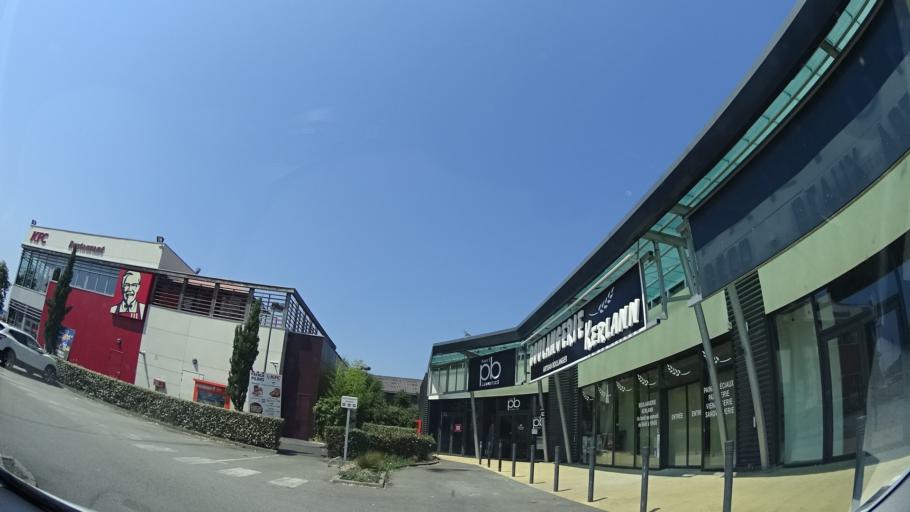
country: FR
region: Brittany
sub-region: Departement du Morbihan
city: Vannes
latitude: 47.6605
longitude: -2.7881
